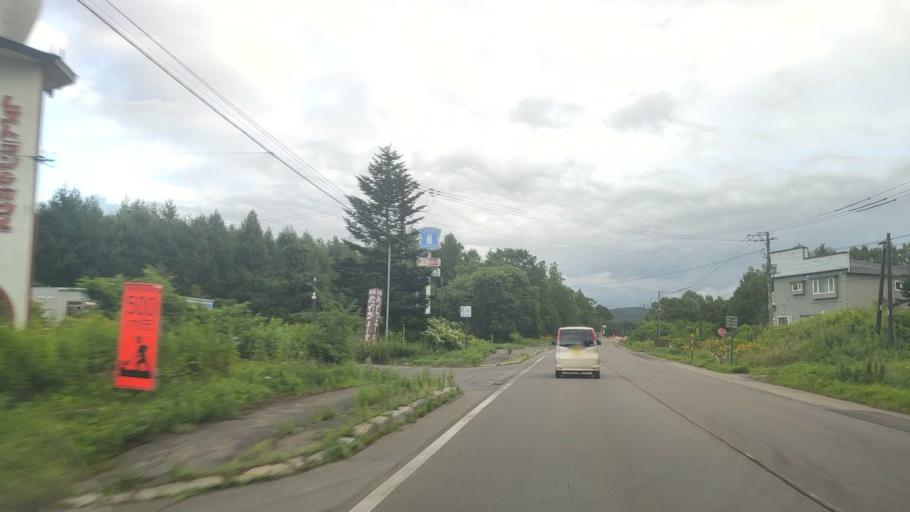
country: JP
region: Hokkaido
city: Nanae
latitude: 41.9986
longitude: 140.6355
